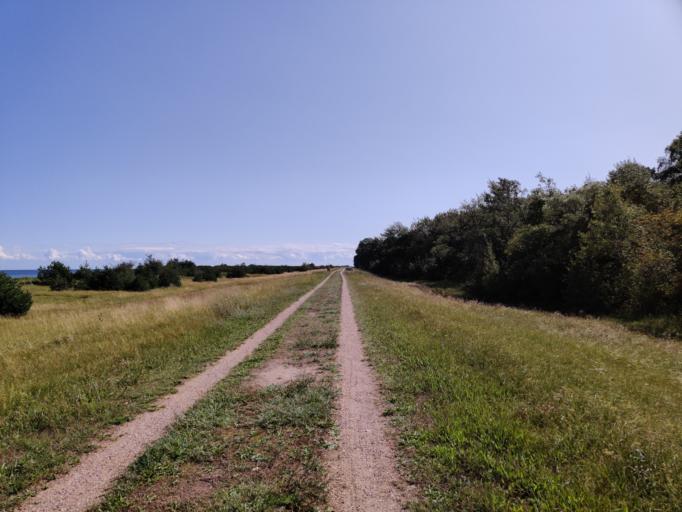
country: DK
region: Zealand
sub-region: Guldborgsund Kommune
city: Nykobing Falster
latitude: 54.6079
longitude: 11.9662
